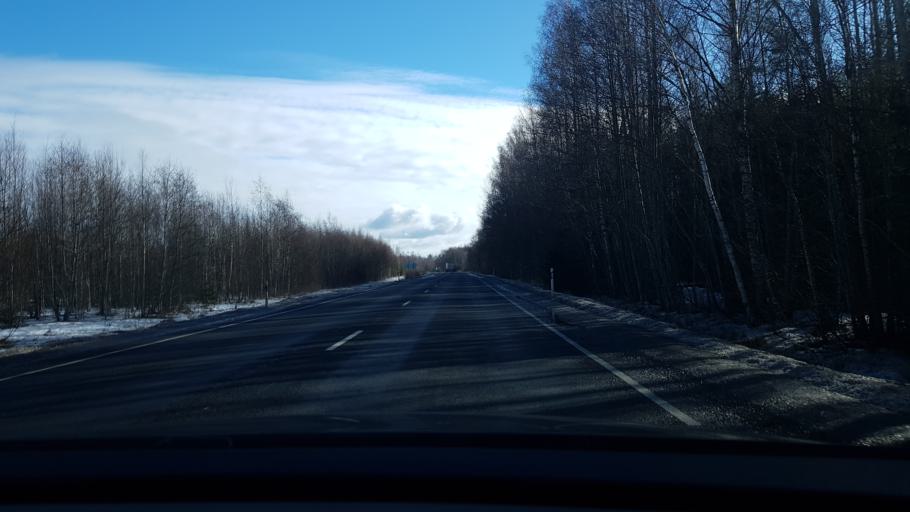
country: EE
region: Paernumaa
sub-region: Paikuse vald
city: Paikuse
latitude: 58.1958
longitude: 24.7484
